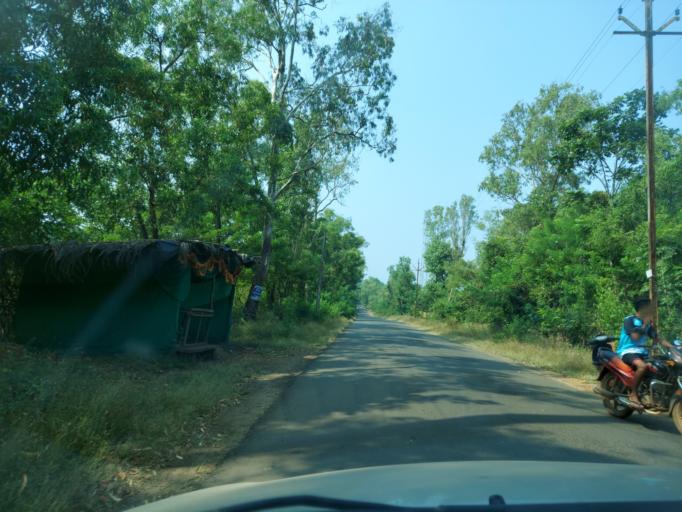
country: IN
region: Maharashtra
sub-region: Sindhudurg
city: Kudal
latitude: 15.9668
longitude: 73.5865
